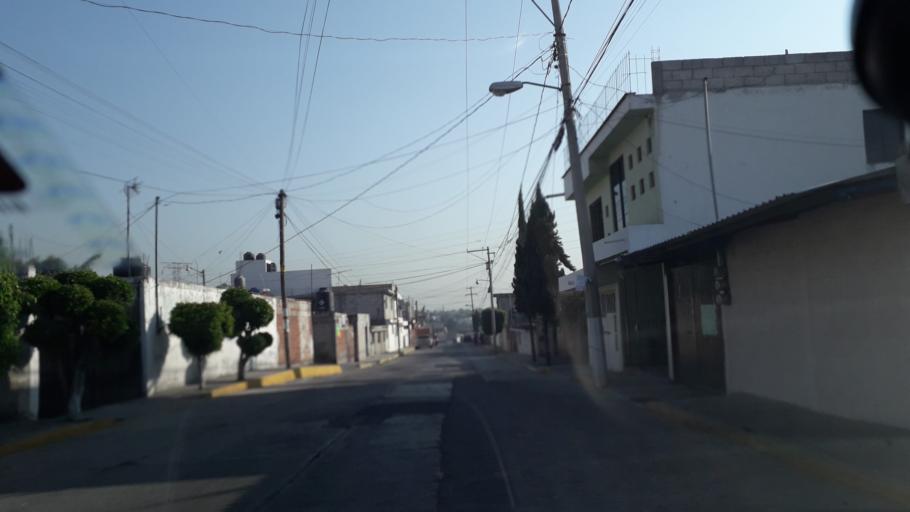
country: MX
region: Puebla
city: Tlazcalancingo
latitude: 19.0368
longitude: -98.2583
